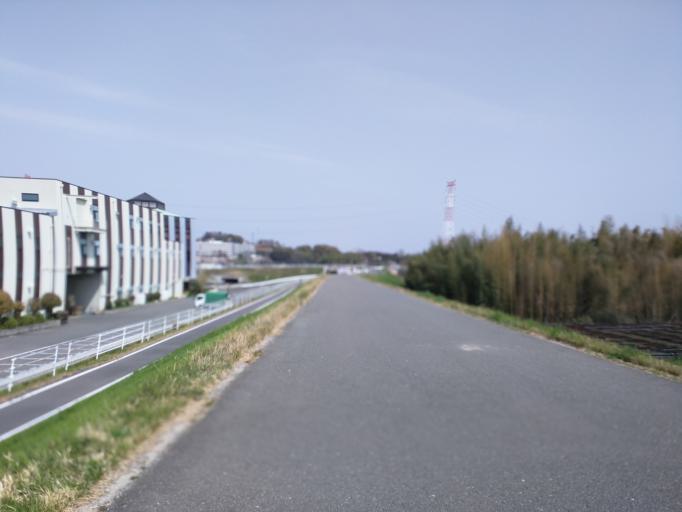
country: JP
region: Kyoto
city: Tanabe
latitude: 34.7970
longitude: 135.7946
